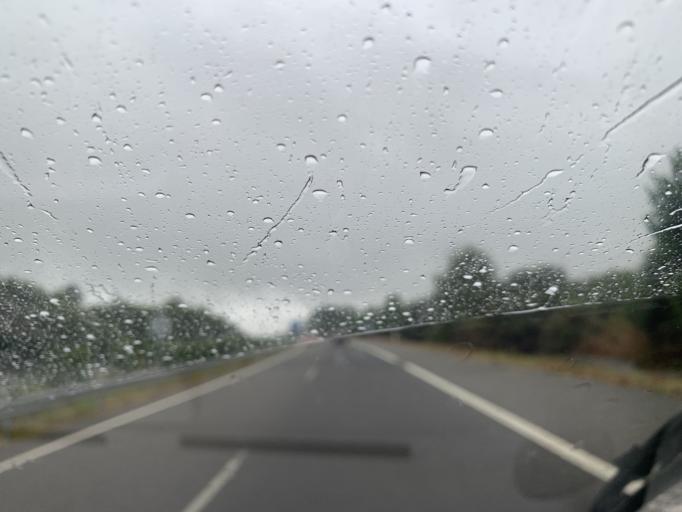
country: ES
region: Galicia
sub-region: Provincia de Lugo
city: Vilalba
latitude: 43.3272
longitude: -7.6142
